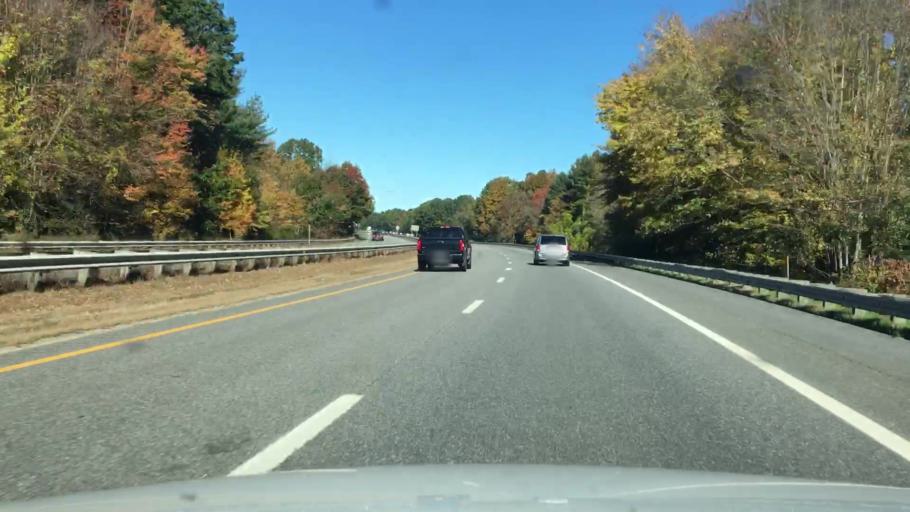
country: US
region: Maine
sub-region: York County
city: Eliot
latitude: 43.1496
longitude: -70.8435
